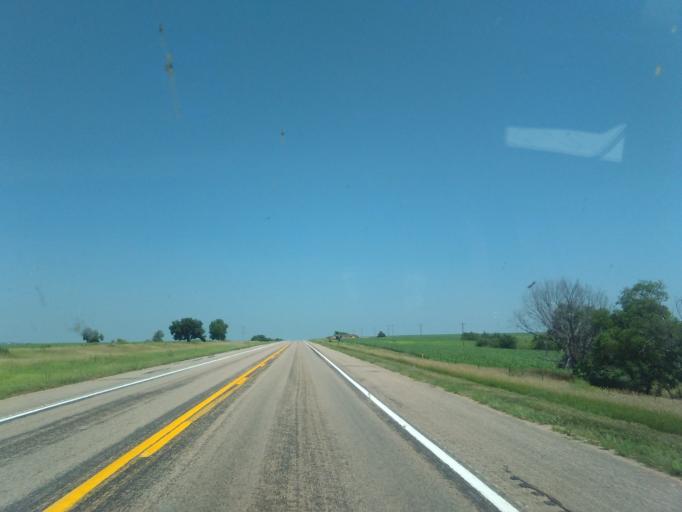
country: US
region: Nebraska
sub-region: Frontier County
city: Stockville
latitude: 40.5995
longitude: -100.6296
